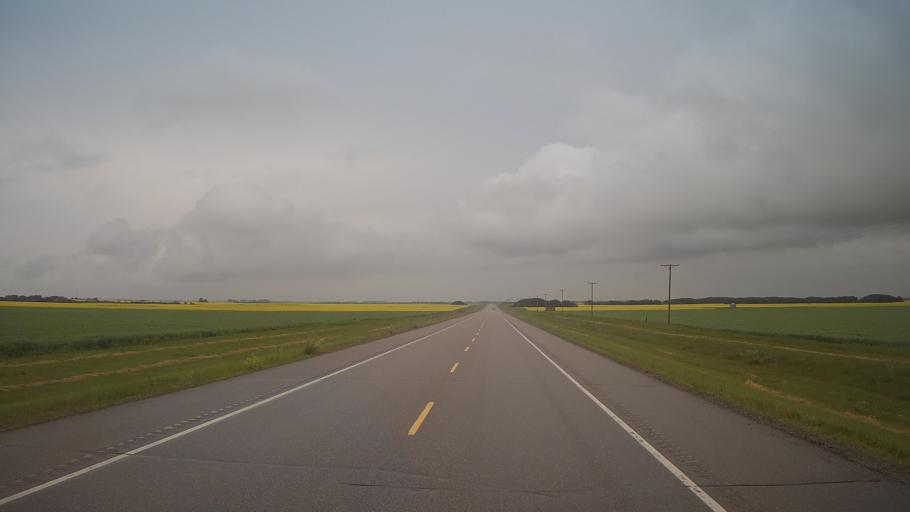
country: CA
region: Saskatchewan
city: Wilkie
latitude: 52.4222
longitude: -108.8995
